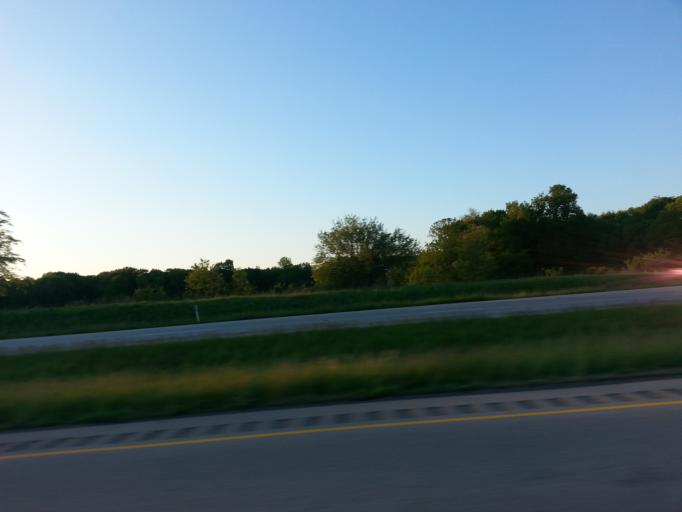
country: US
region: Indiana
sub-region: Fountain County
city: Veedersburg
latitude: 40.1243
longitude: -87.2375
